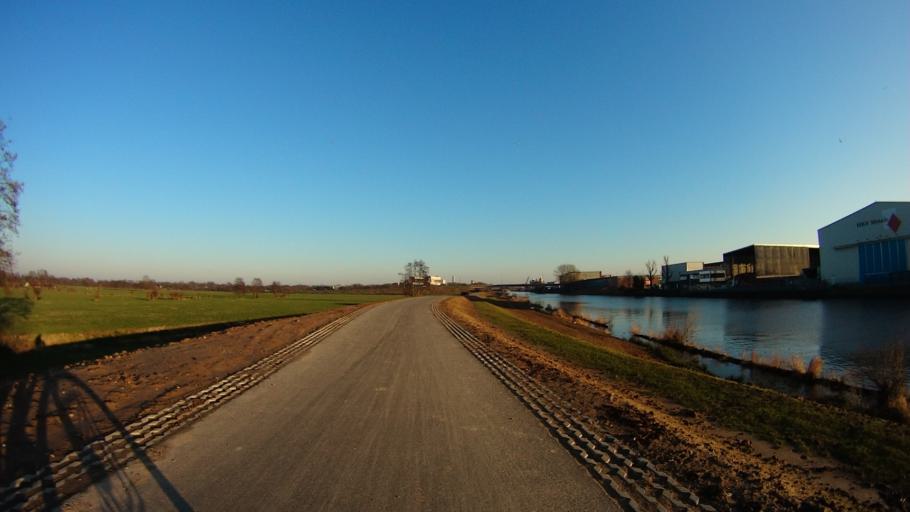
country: NL
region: Utrecht
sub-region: Gemeente Amersfoort
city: Hoogland
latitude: 52.1738
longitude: 5.3574
